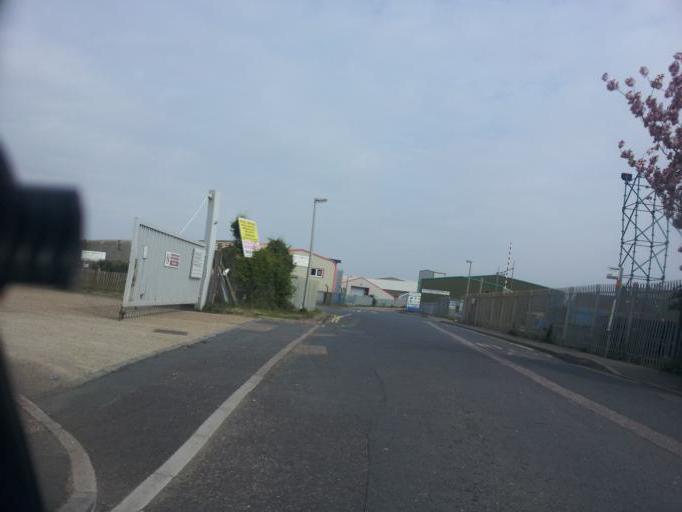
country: GB
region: England
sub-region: Medway
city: Rochester
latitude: 51.3977
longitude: 0.5074
